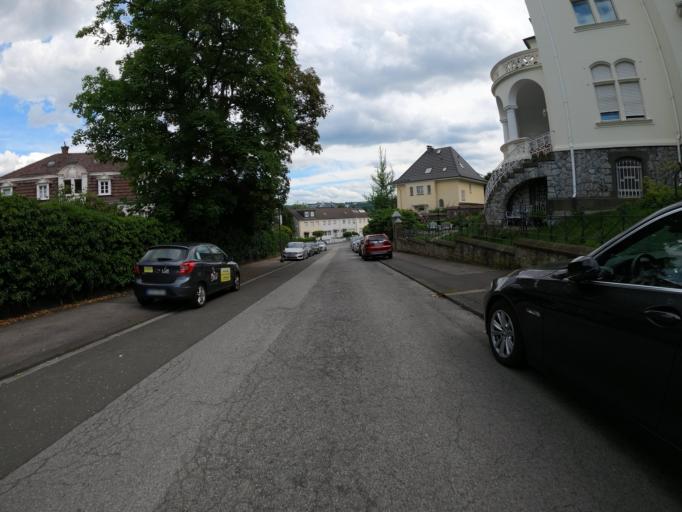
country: DE
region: North Rhine-Westphalia
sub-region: Regierungsbezirk Dusseldorf
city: Wuppertal
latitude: 51.2565
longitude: 7.1273
